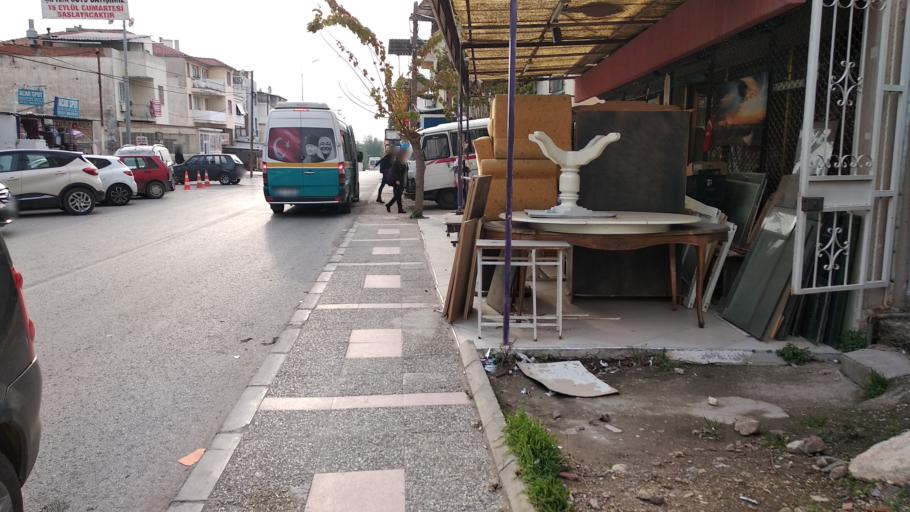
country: TR
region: Izmir
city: Karsiyaka
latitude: 38.4936
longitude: 27.0736
